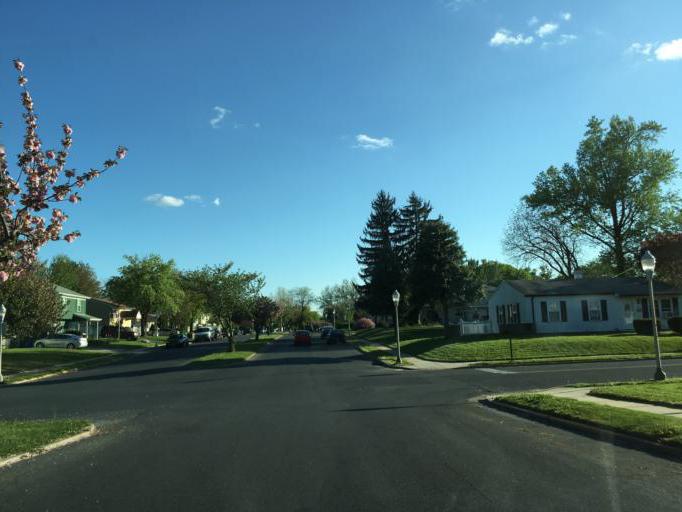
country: US
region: Maryland
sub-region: Frederick County
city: Frederick
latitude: 39.4077
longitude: -77.4185
